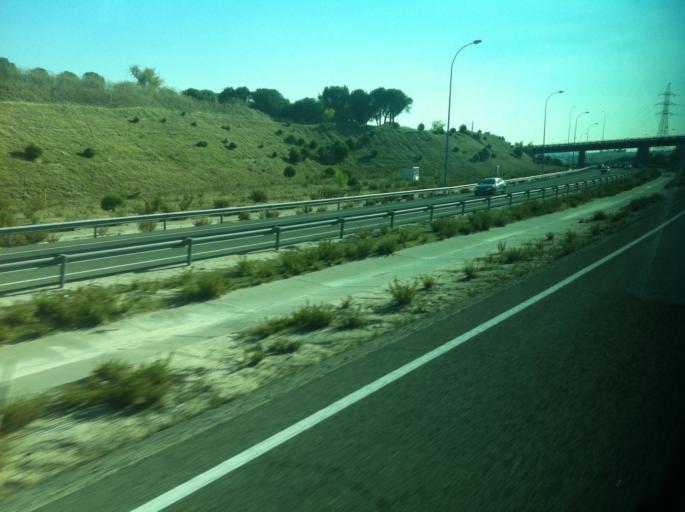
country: ES
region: Madrid
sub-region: Provincia de Madrid
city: San Sebastian de los Reyes
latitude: 40.5264
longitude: -3.5966
